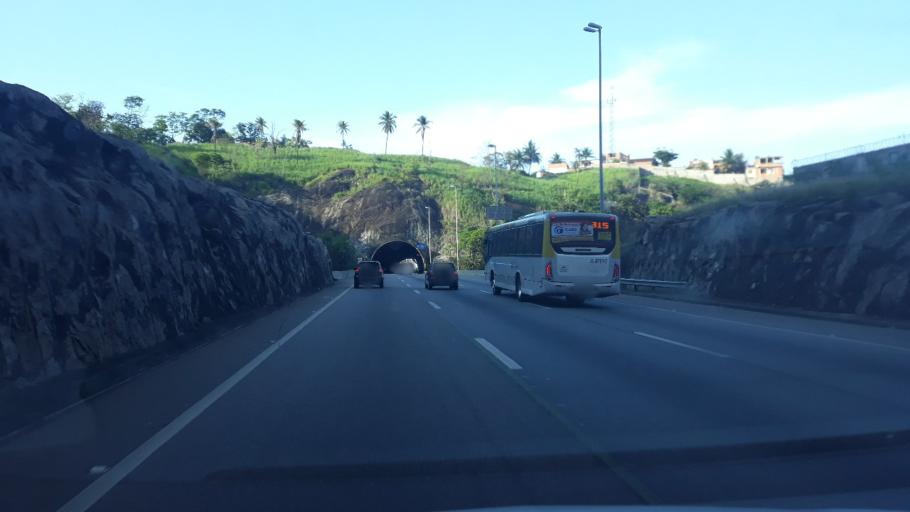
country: BR
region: Rio de Janeiro
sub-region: Sao Joao De Meriti
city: Sao Joao de Meriti
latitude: -22.9319
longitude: -43.3448
